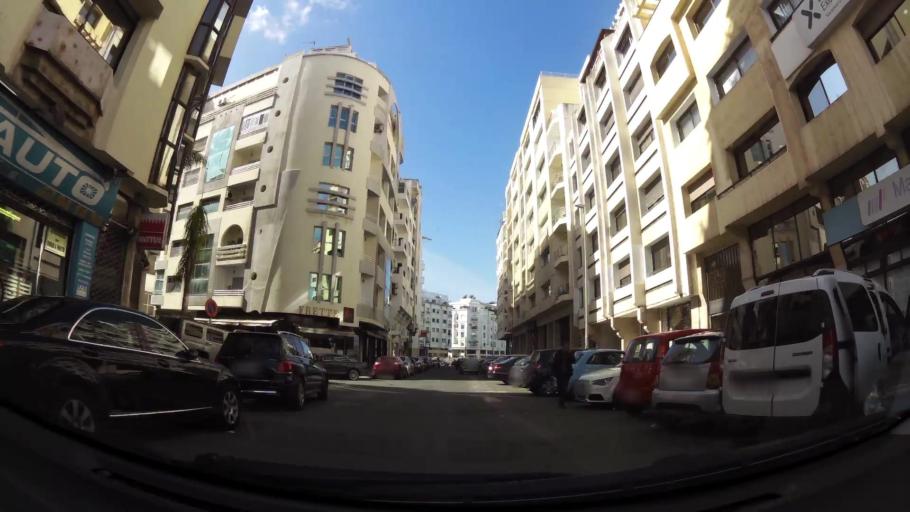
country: MA
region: Grand Casablanca
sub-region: Casablanca
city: Casablanca
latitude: 33.5904
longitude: -7.6363
